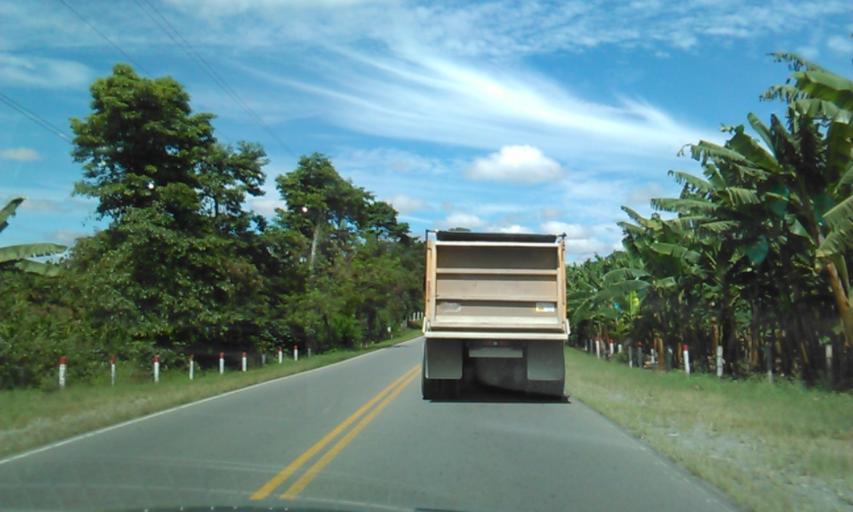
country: CO
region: Quindio
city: Cordoba
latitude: 4.4397
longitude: -75.7178
